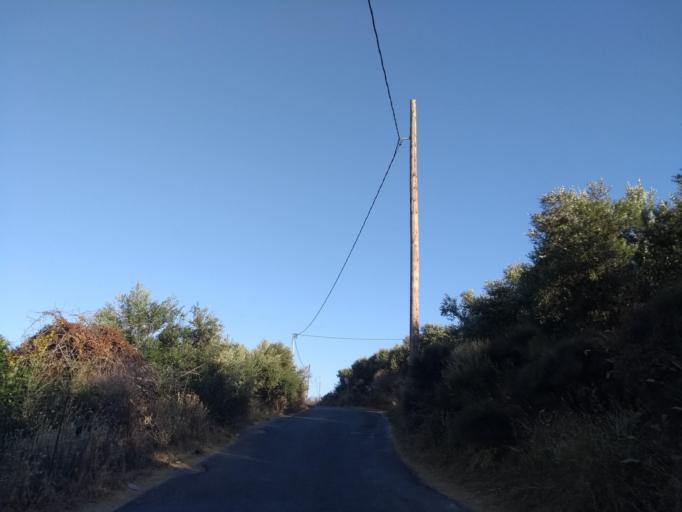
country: GR
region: Crete
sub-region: Nomos Chanias
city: Kalivai
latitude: 35.4326
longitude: 24.1757
